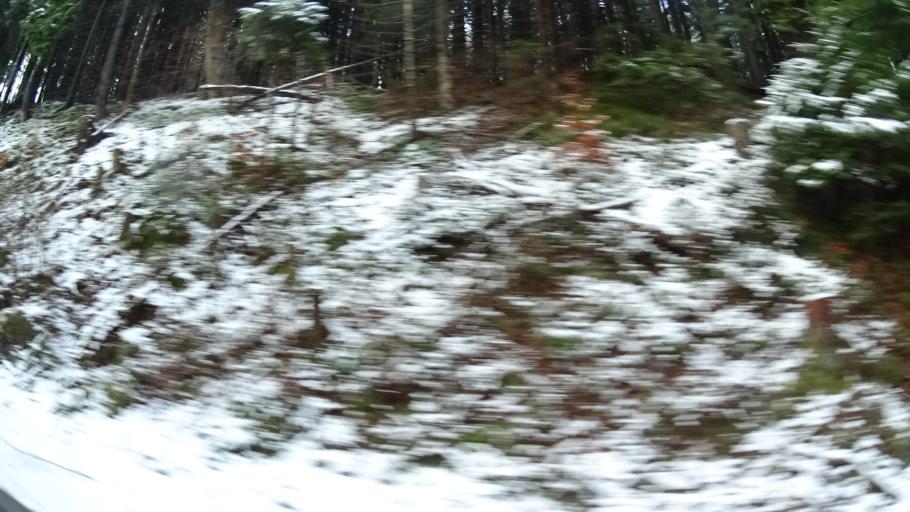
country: DE
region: Thuringia
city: Frankenhain
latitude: 50.7614
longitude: 10.7698
